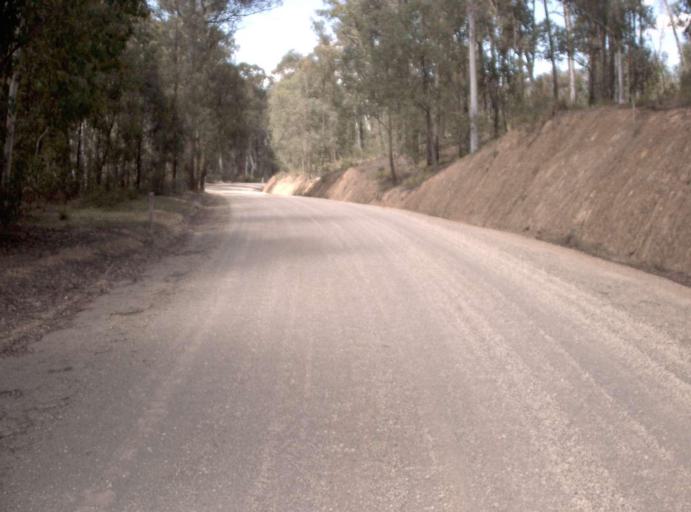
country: AU
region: New South Wales
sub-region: Bombala
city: Bombala
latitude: -37.1814
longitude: 148.7116
